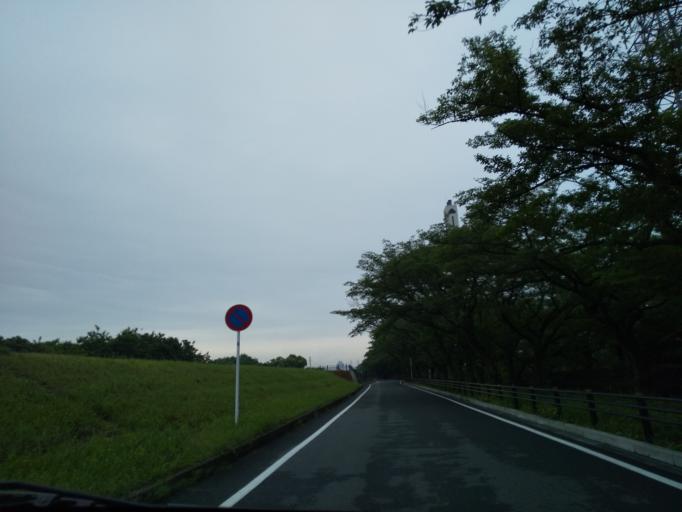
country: JP
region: Tokyo
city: Hino
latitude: 35.6681
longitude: 139.4282
